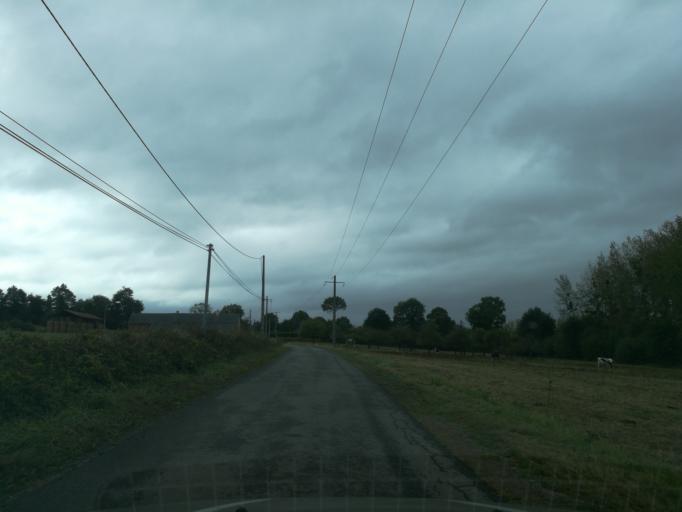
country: FR
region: Brittany
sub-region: Departement d'Ille-et-Vilaine
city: Pleumeleuc
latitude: 48.1808
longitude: -1.9002
